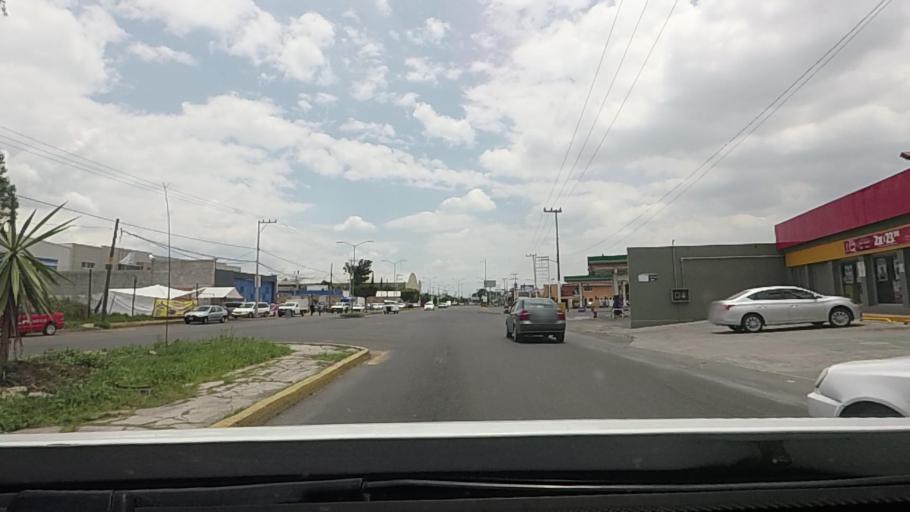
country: MX
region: Mexico
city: Chalco de Diaz Covarrubias
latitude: 19.2535
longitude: -98.8817
